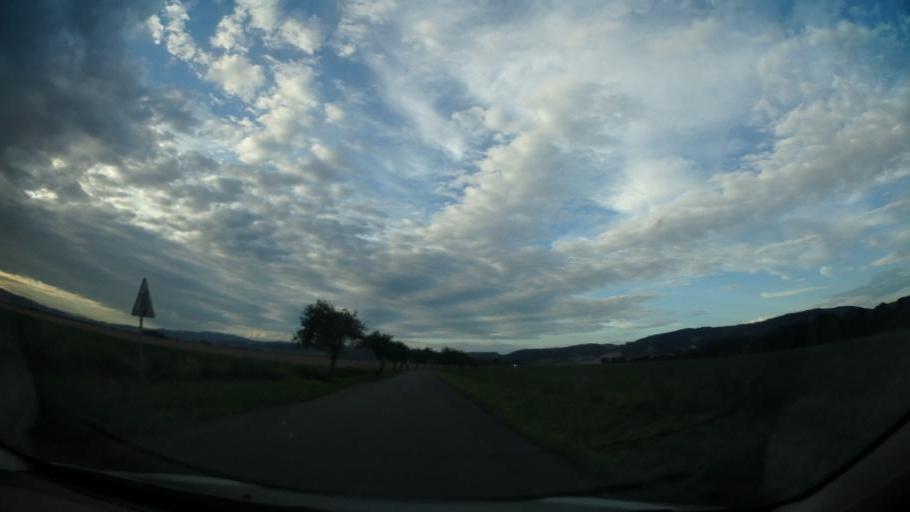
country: CZ
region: Olomoucky
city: Ujezd
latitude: 49.7867
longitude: 17.1896
